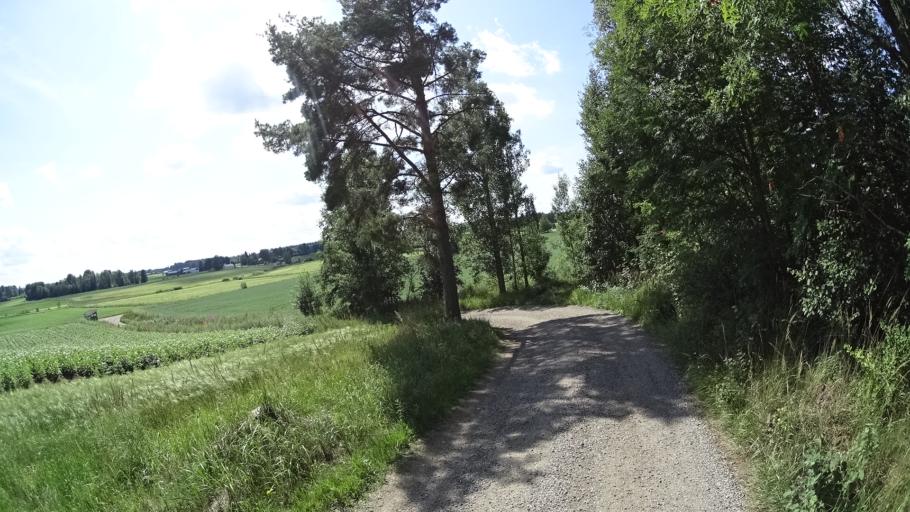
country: FI
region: Haeme
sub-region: Forssa
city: Tammela
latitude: 60.7638
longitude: 23.8869
